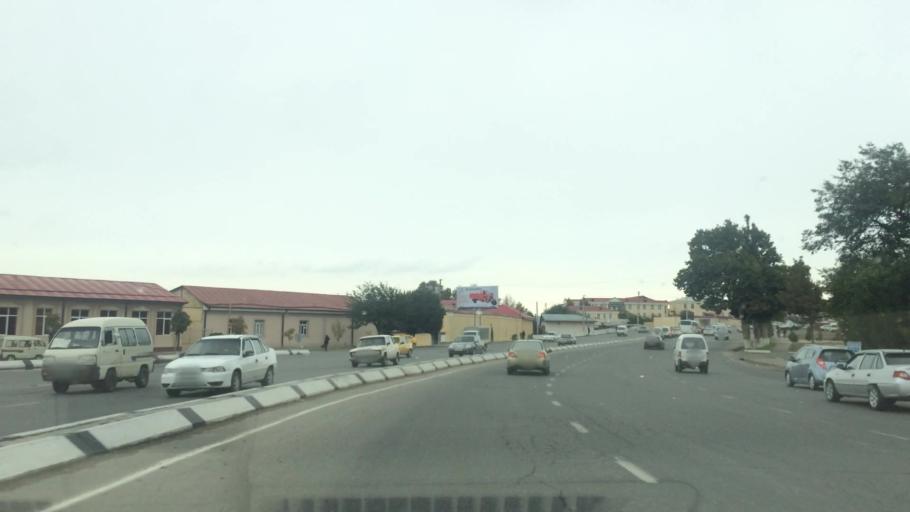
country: UZ
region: Samarqand
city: Samarqand
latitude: 39.6766
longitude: 67.0070
